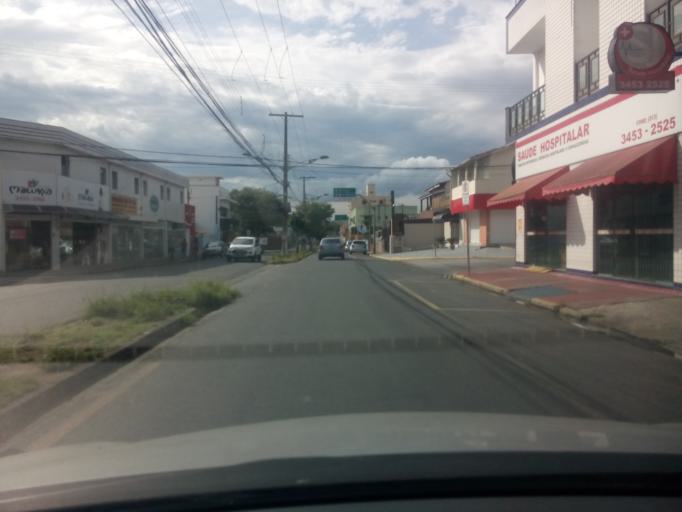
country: BR
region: Sao Paulo
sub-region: Peruibe
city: Peruibe
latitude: -24.3207
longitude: -46.9972
